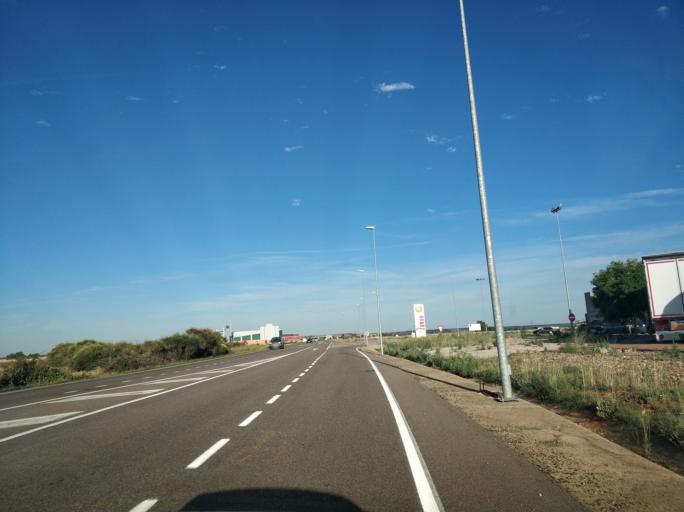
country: ES
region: Castille and Leon
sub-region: Provincia de Leon
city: Villamanan
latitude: 42.3244
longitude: -5.6013
